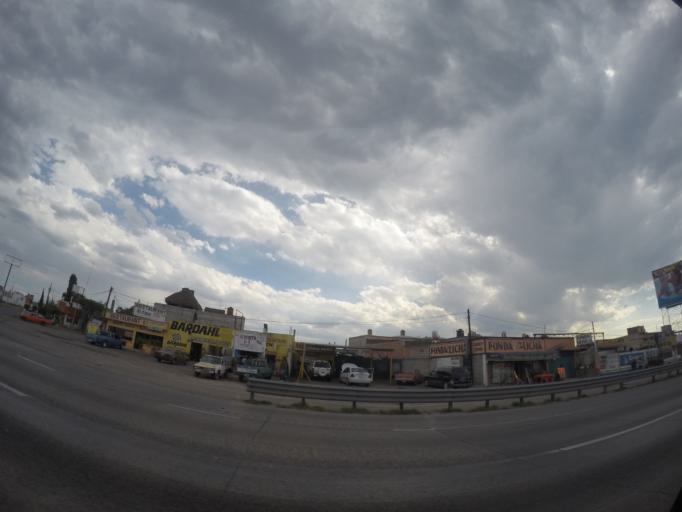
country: MX
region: Queretaro
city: San Juan del Rio
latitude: 20.3688
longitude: -99.9825
